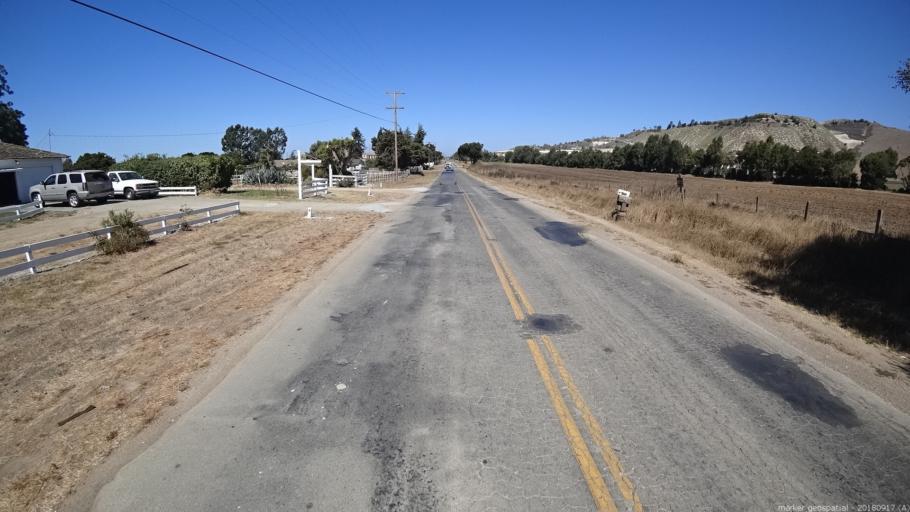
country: US
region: California
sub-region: Monterey County
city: Prunedale
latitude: 36.7365
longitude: -121.5995
